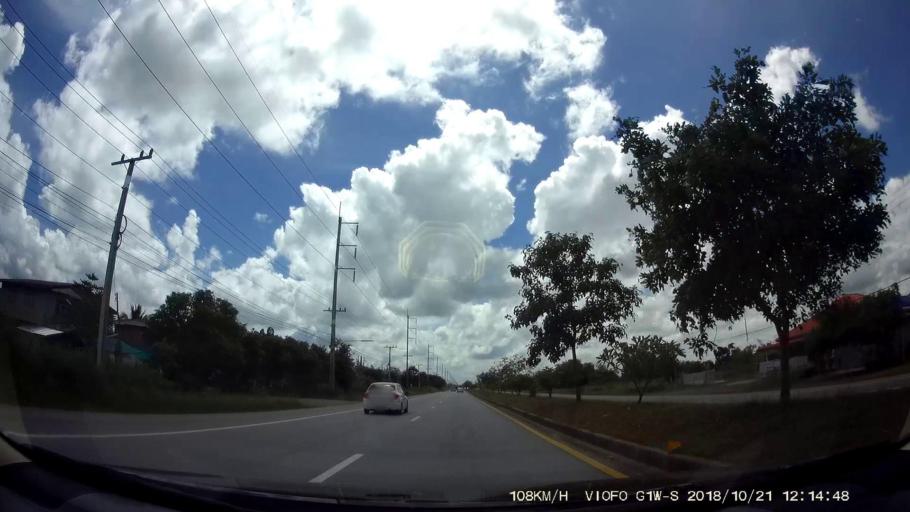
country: TH
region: Nakhon Ratchasima
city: Dan Khun Thot
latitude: 15.3716
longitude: 101.8333
